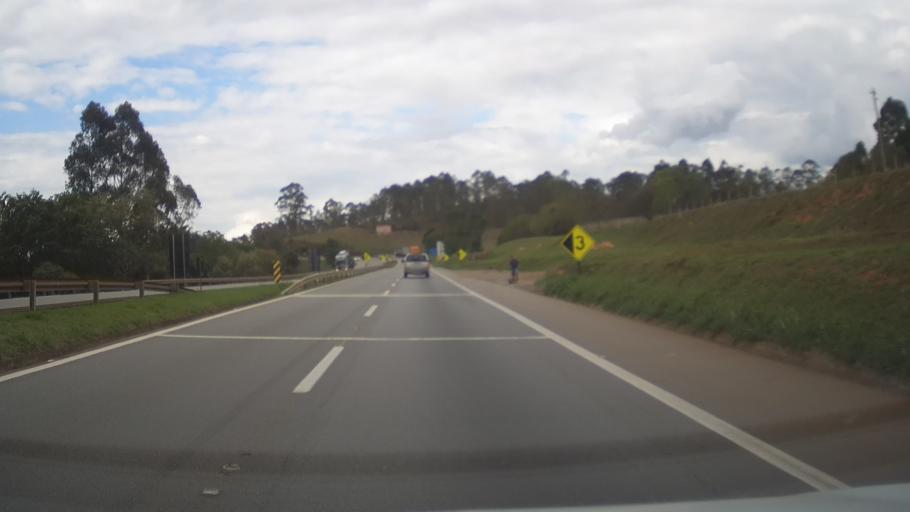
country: BR
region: Minas Gerais
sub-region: Itauna
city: Itauna
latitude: -20.3023
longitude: -44.4439
